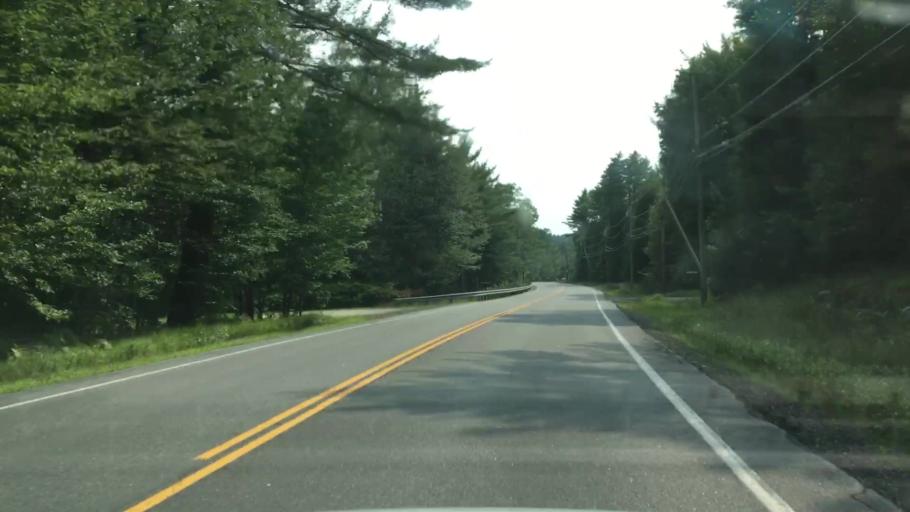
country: US
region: Maine
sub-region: Oxford County
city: South Paris
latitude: 44.2289
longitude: -70.4953
